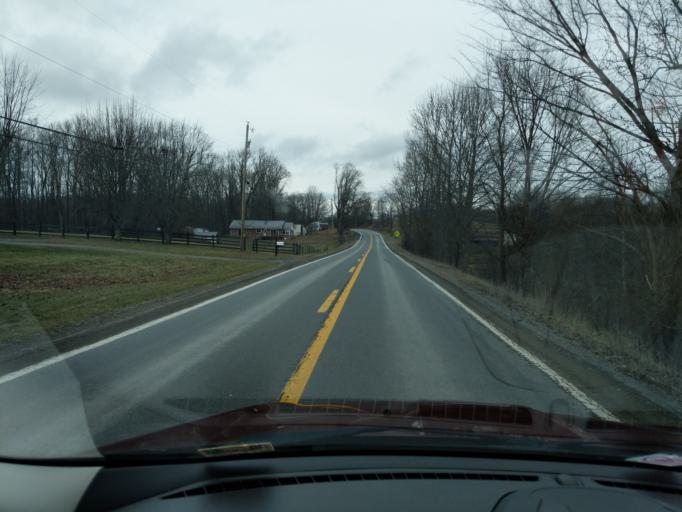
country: US
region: West Virginia
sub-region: Greenbrier County
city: Lewisburg
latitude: 37.8473
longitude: -80.5510
